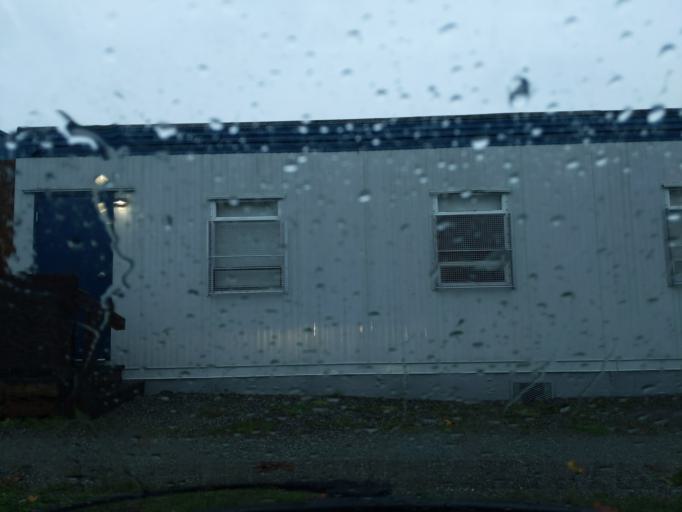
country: CA
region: British Columbia
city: New Westminster
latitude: 49.1936
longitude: -122.8590
